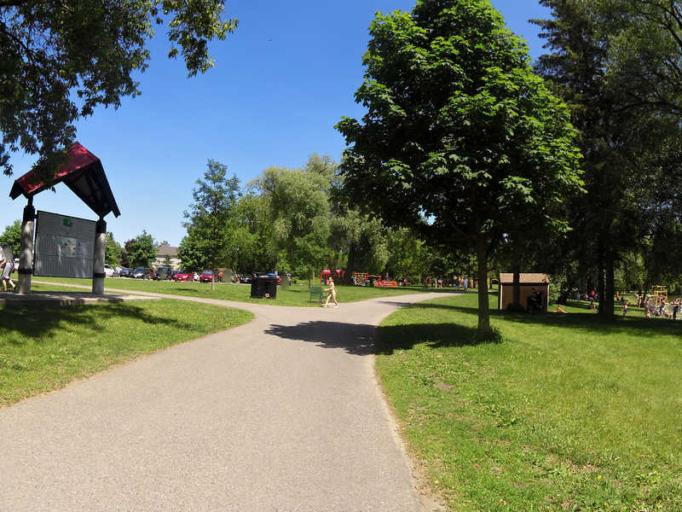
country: CA
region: Ontario
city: Peterborough
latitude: 44.3002
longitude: -78.3070
